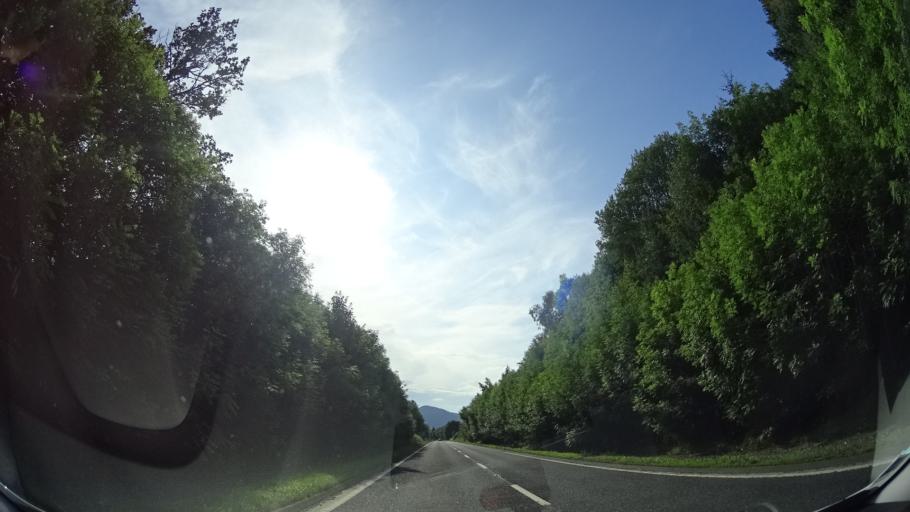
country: GB
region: Scotland
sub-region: Highland
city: Muir of Ord
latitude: 57.5585
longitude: -4.5230
